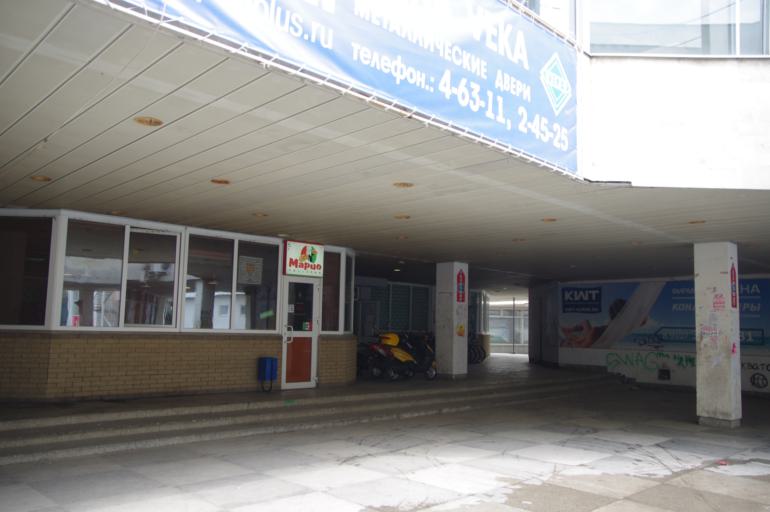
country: RU
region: Kursk
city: Kurchatov
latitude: 51.6601
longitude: 35.6584
